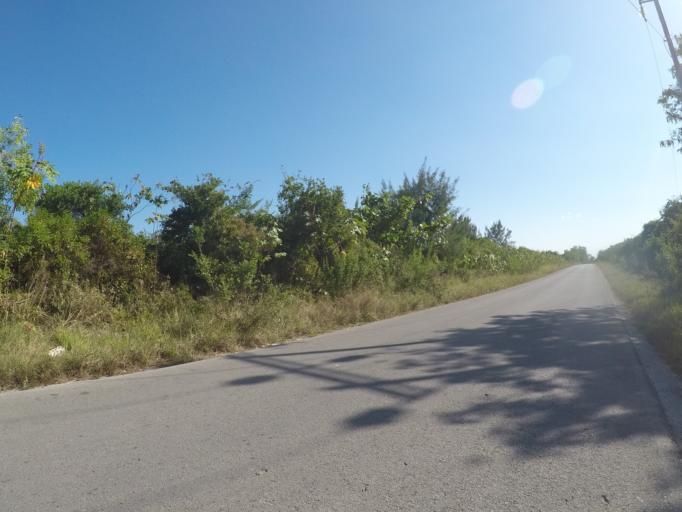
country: TZ
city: Kiwengwa
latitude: -6.1434
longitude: 39.5070
